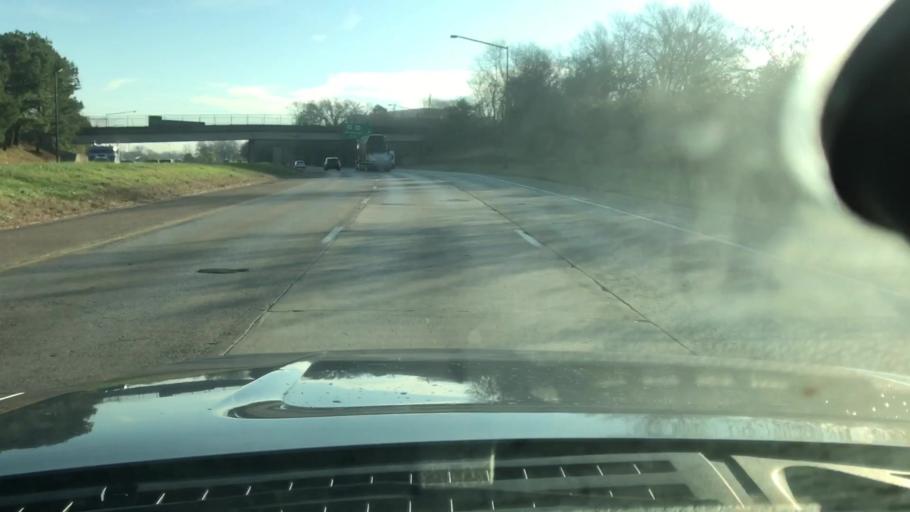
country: US
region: Tennessee
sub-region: Davidson County
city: Oak Hill
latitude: 36.1215
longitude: -86.7577
